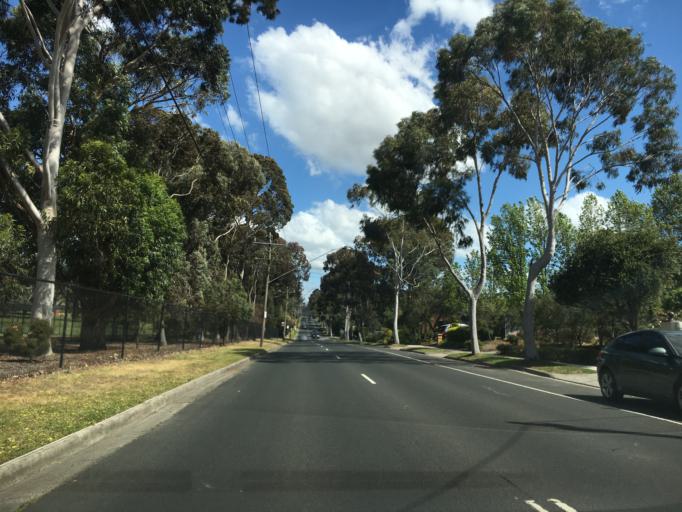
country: AU
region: Victoria
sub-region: Monash
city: Mulgrave
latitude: -37.8926
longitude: 145.1917
